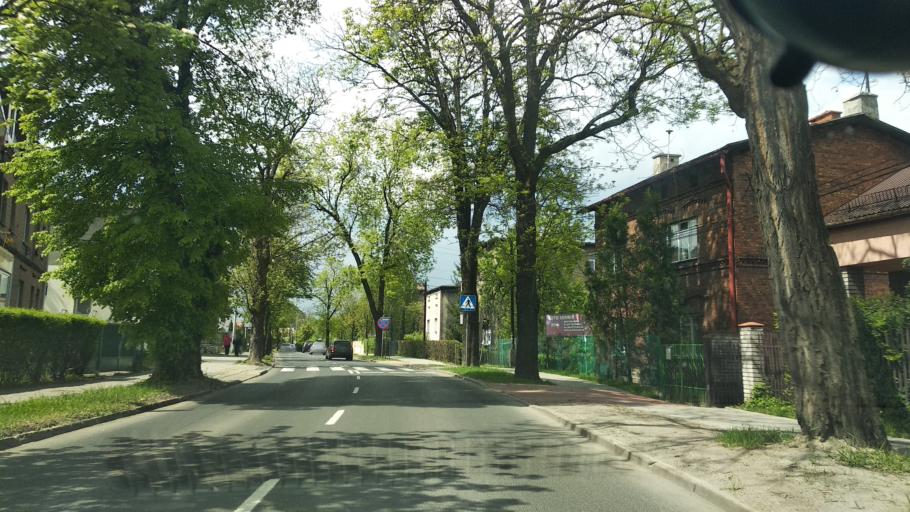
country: PL
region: Silesian Voivodeship
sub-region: Katowice
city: Katowice
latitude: 50.2292
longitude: 18.9563
